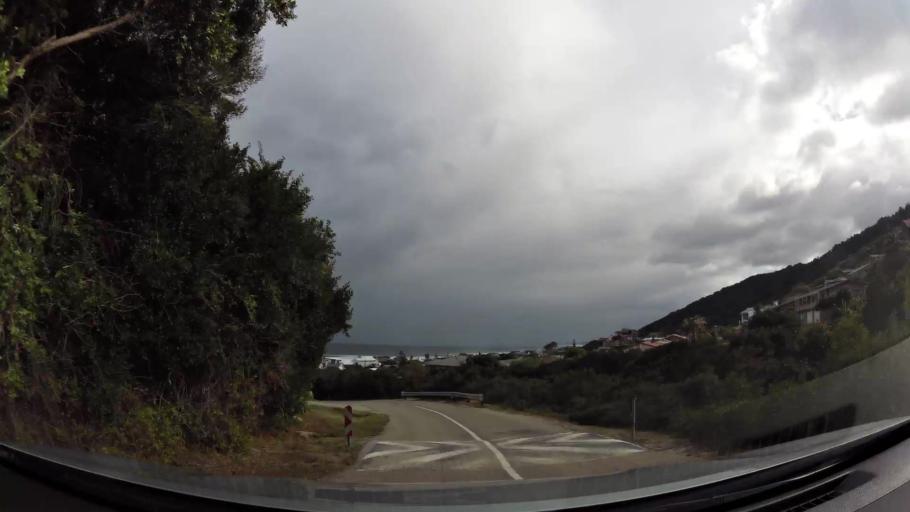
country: ZA
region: Western Cape
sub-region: Eden District Municipality
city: George
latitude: -34.0482
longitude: 22.3160
